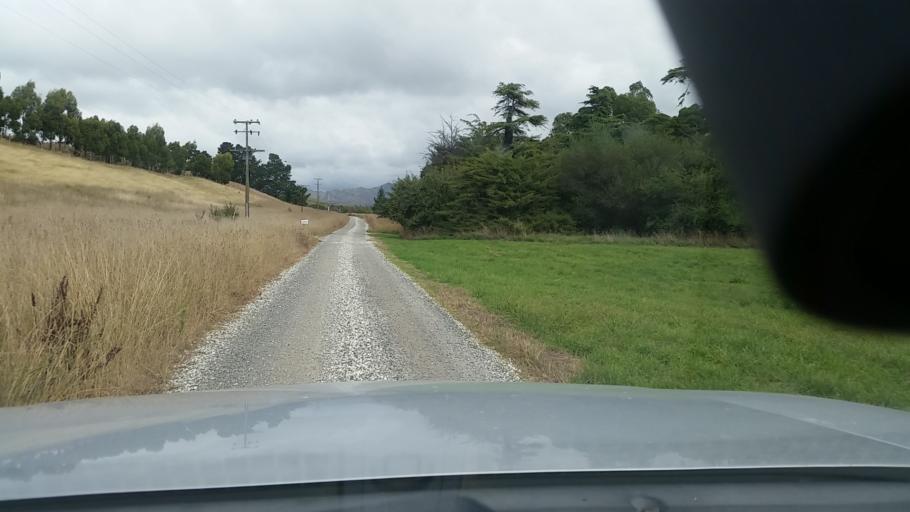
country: NZ
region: Marlborough
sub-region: Marlborough District
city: Blenheim
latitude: -41.6872
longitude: 174.1273
